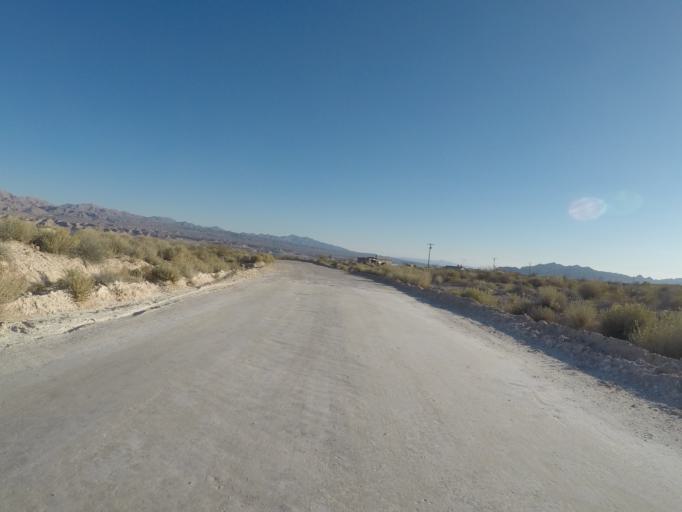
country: US
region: Nevada
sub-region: Clark County
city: Moapa Valley
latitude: 36.3824
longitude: -114.4085
